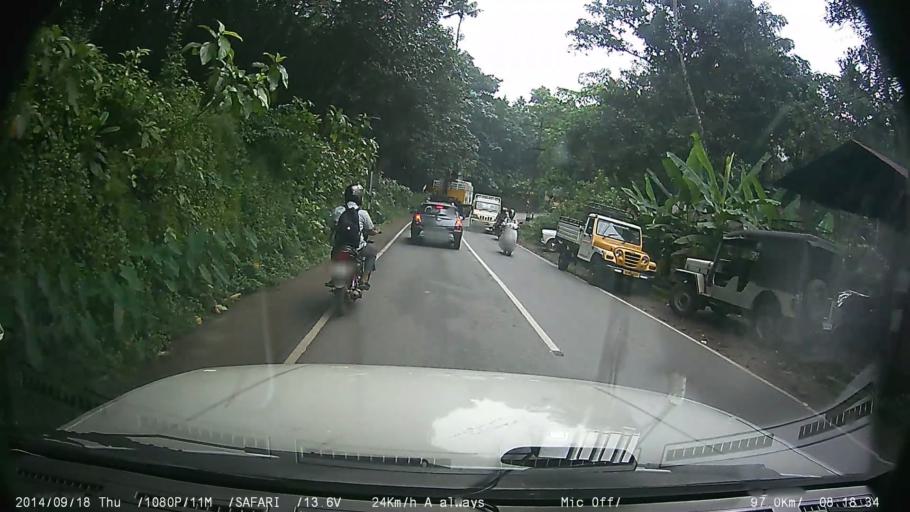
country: IN
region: Kerala
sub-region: Kottayam
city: Palackattumala
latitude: 9.6477
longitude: 76.6101
